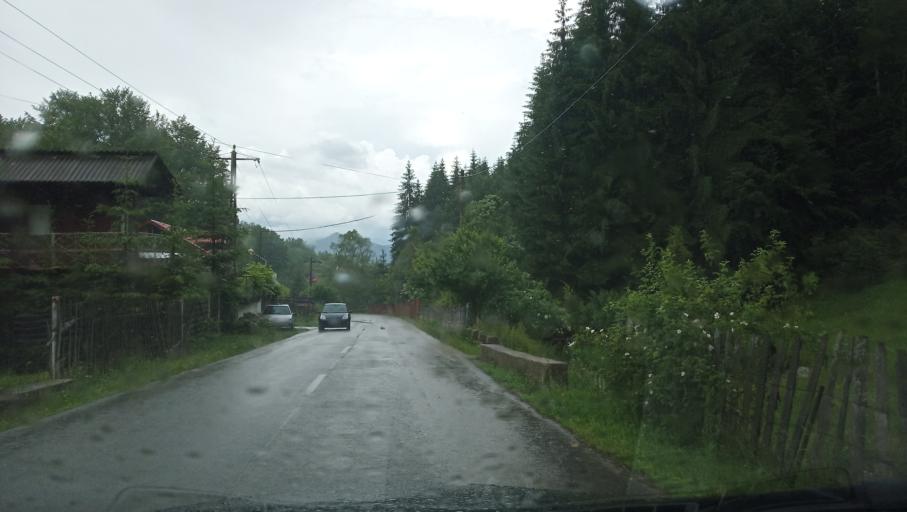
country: RO
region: Hunedoara
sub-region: Oras Petrila
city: Petrila
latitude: 45.3987
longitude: 23.4173
